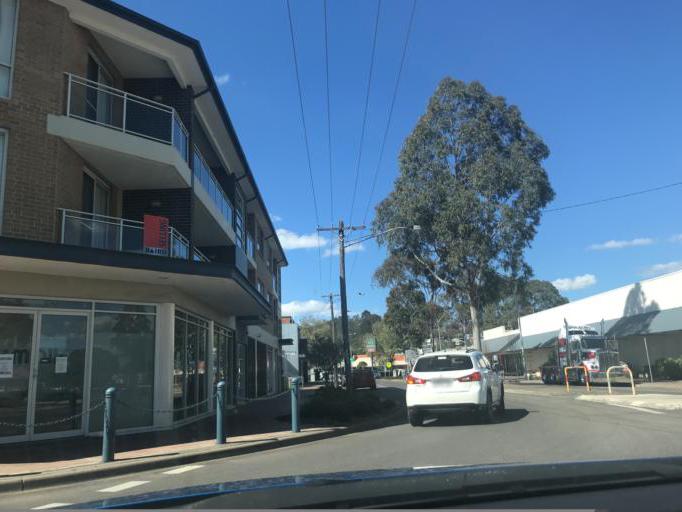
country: AU
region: New South Wales
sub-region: Cessnock
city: Cessnock
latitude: -32.8356
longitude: 151.3534
